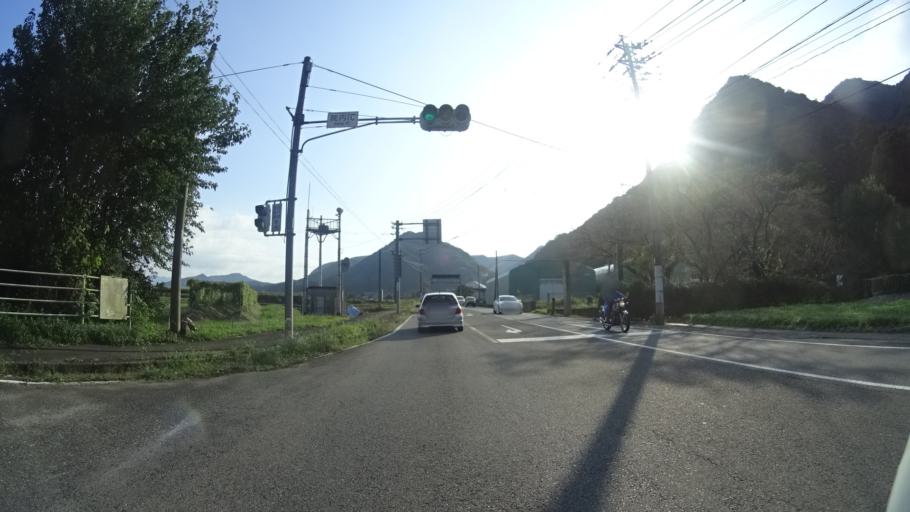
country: JP
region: Oita
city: Bungo-Takada-shi
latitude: 33.4781
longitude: 131.3327
